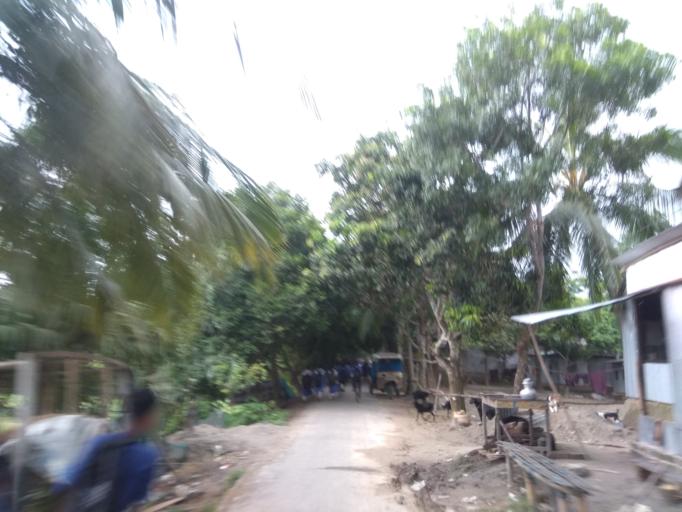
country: BD
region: Dhaka
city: Dohar
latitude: 23.4857
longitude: 90.0252
